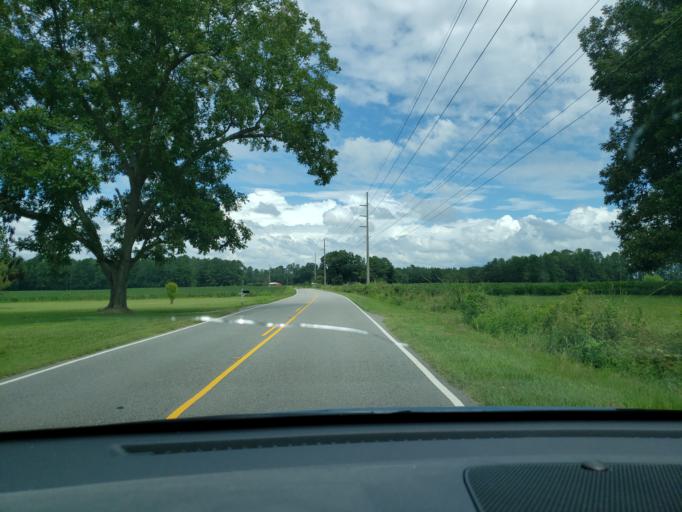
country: US
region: North Carolina
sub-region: Columbus County
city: Tabor City
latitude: 34.1623
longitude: -78.7819
